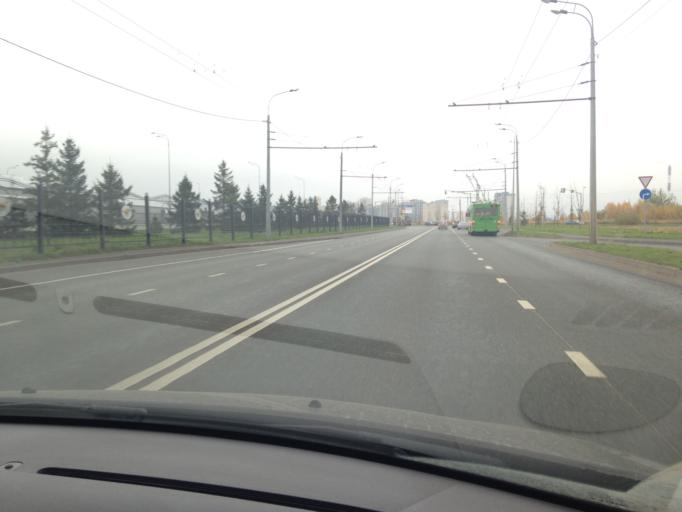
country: RU
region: Tatarstan
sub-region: Gorod Kazan'
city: Kazan
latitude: 55.7835
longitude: 49.1968
